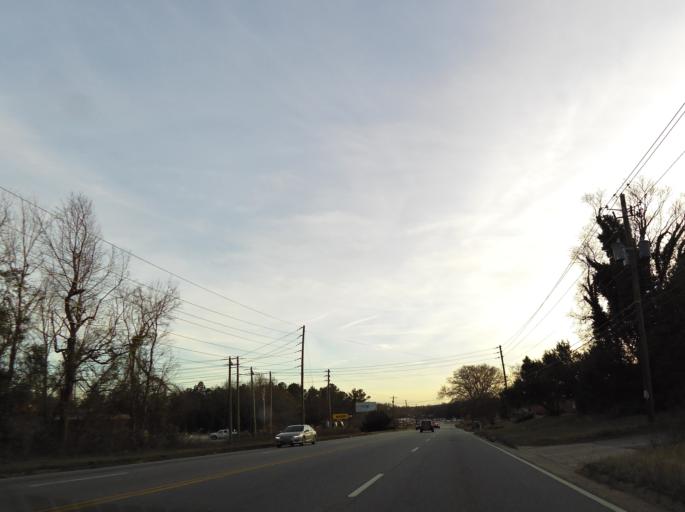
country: US
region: Georgia
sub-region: Bibb County
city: Macon
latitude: 32.7756
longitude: -83.6575
